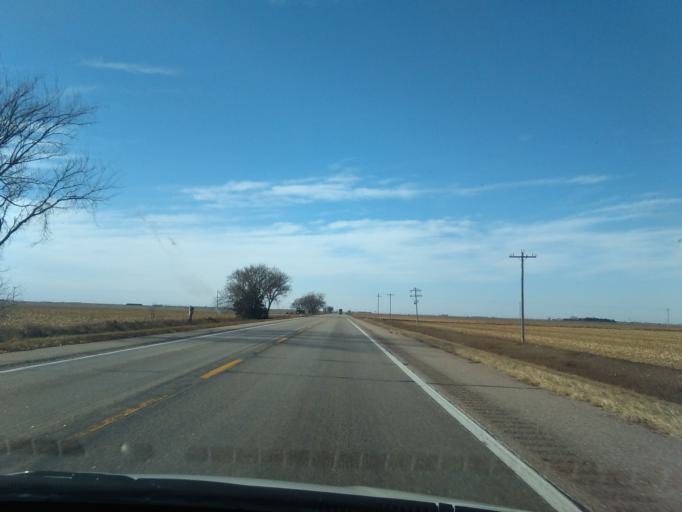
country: US
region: Nebraska
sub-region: Clay County
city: Harvard
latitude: 40.5828
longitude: -98.0864
